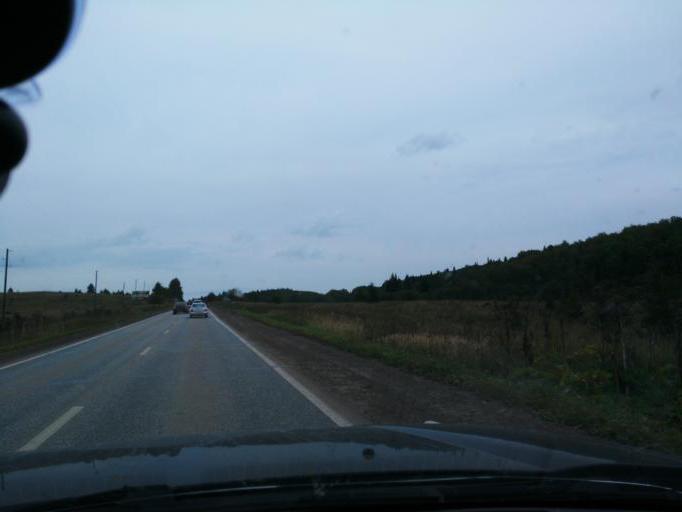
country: RU
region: Perm
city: Chernushka
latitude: 56.5734
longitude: 56.1299
